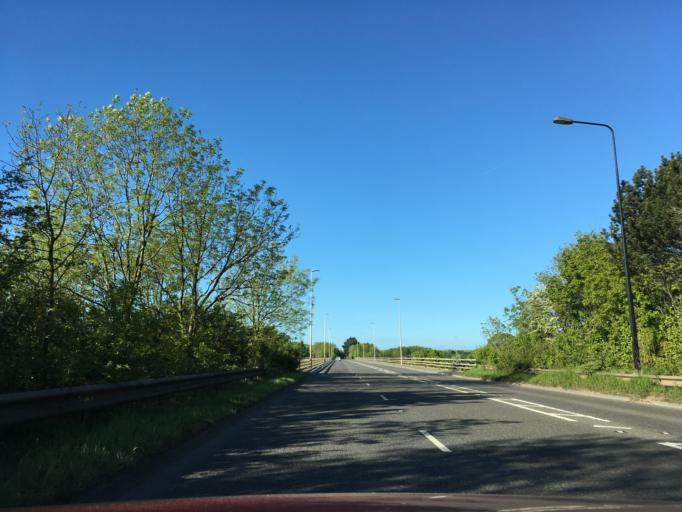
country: GB
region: England
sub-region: North Somerset
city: Long Ashton
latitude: 51.4293
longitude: -2.6476
